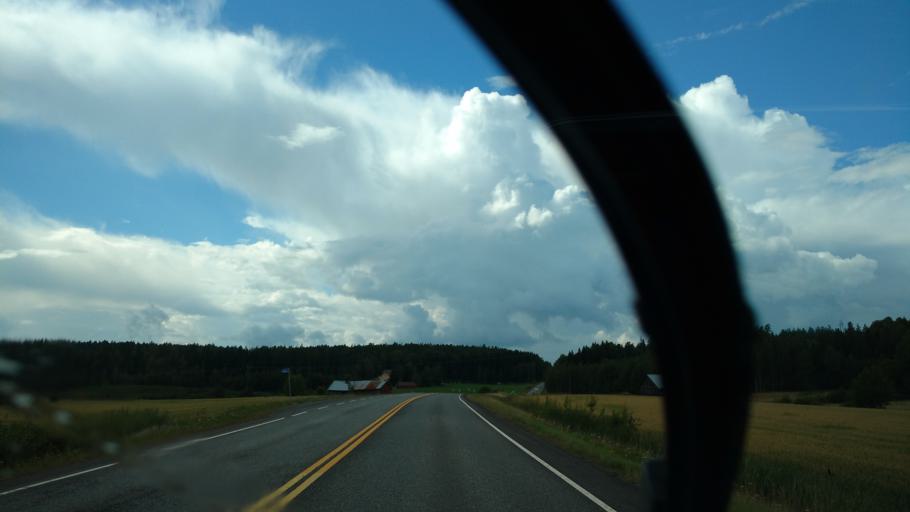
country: FI
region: Varsinais-Suomi
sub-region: Turku
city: Paimio
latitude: 60.4089
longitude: 22.7942
